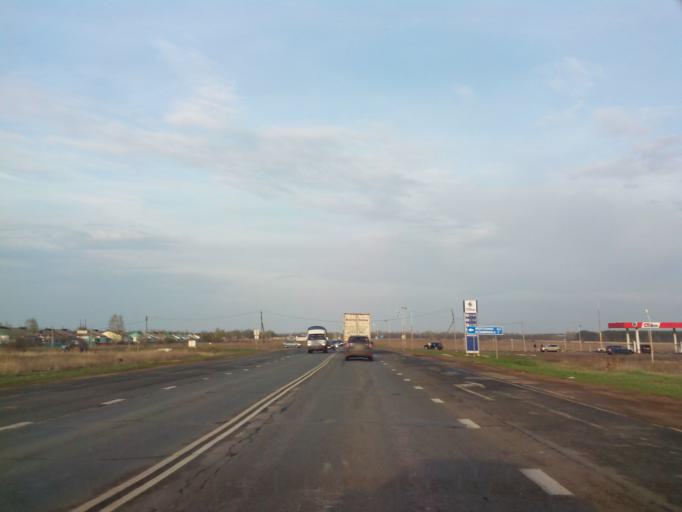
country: RU
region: Rjazan
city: Zarechnyy
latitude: 53.7522
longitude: 39.8072
